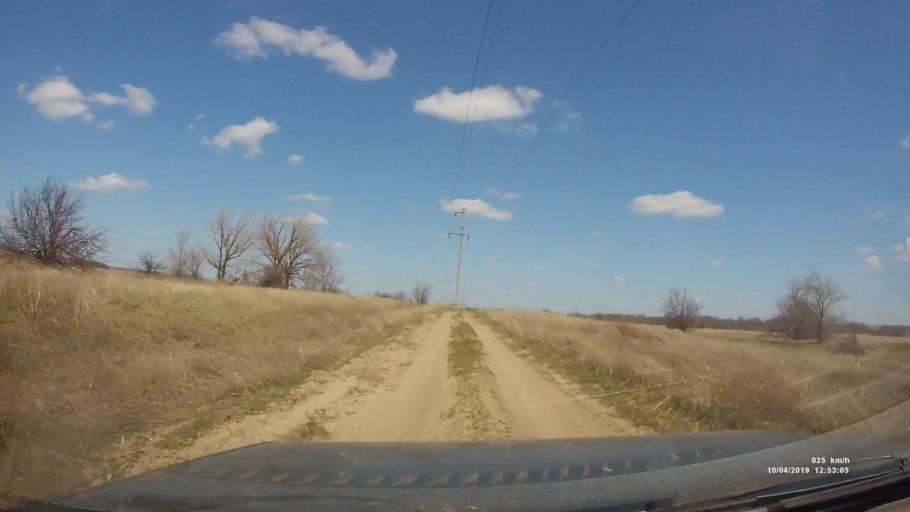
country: RU
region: Rostov
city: Masalovka
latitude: 48.3630
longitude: 40.2198
